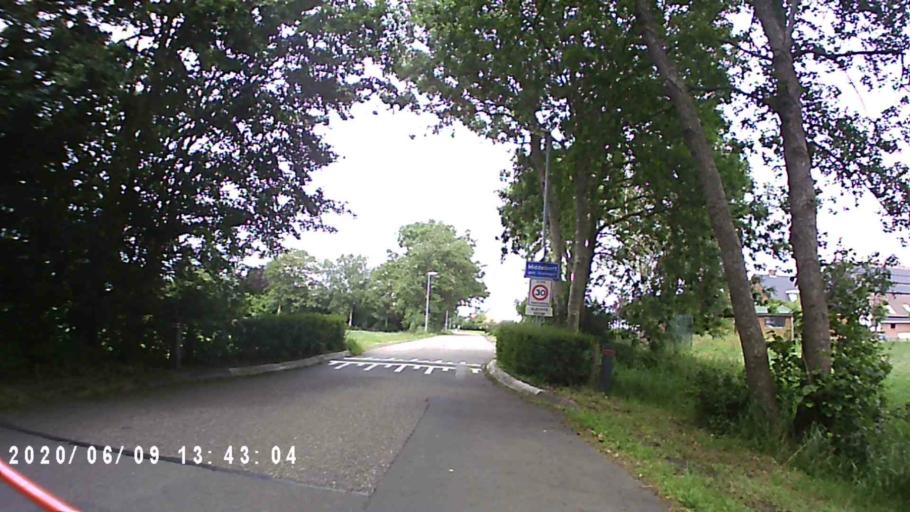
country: NL
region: Groningen
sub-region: Gemeente Haren
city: Haren
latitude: 53.2155
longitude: 6.6420
